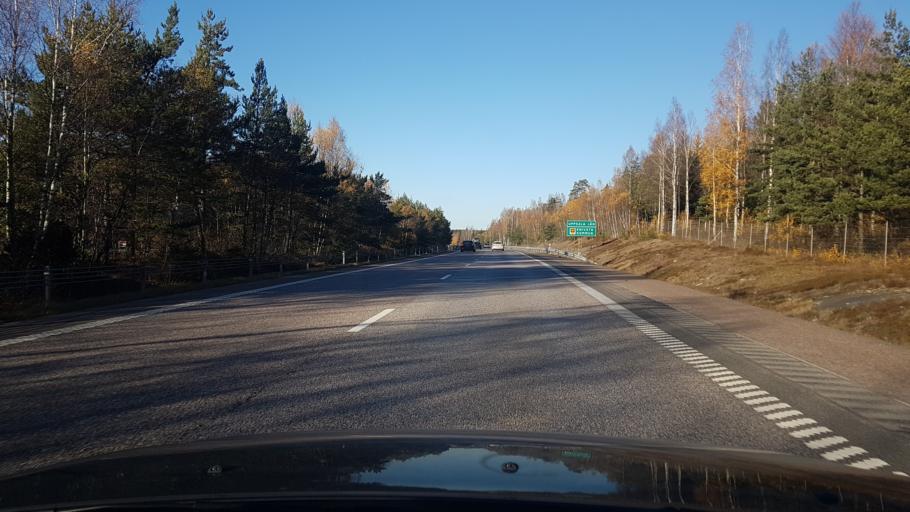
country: SE
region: Stockholm
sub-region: Sigtuna Kommun
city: Marsta
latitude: 59.6980
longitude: 17.8637
